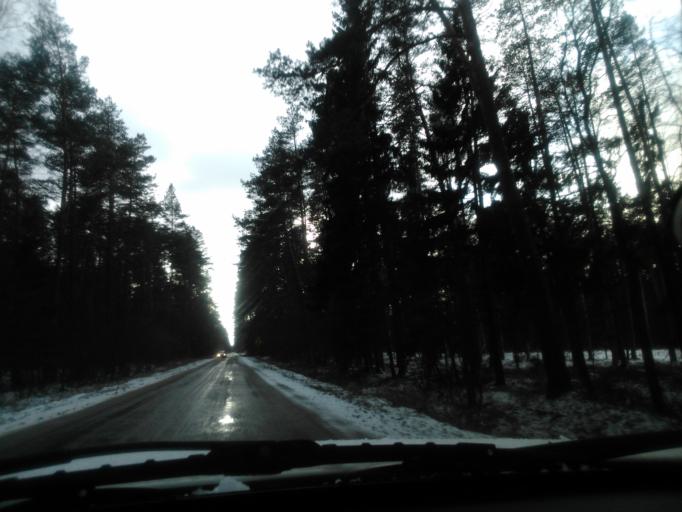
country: PL
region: Kujawsko-Pomorskie
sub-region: Powiat wabrzeski
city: Debowa Laka
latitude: 53.1719
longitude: 19.1372
